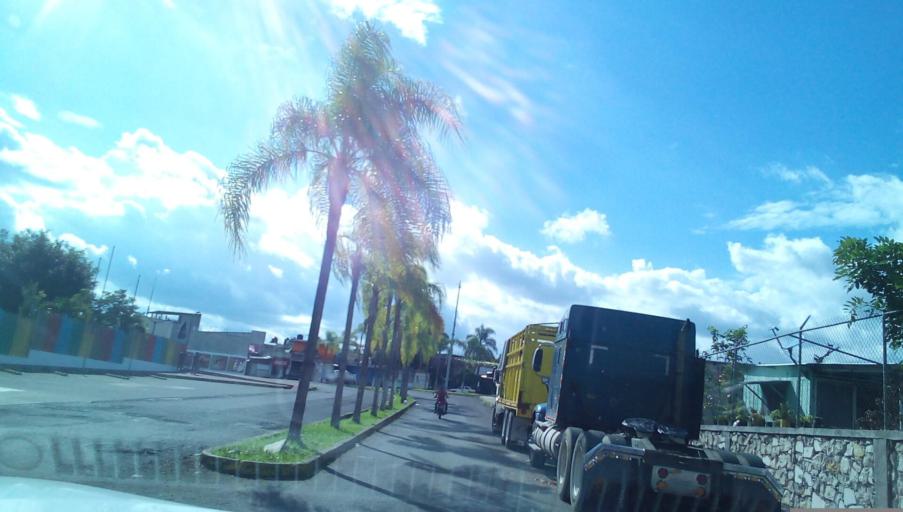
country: MX
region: Veracruz
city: Cordoba
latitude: 18.8889
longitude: -96.9214
